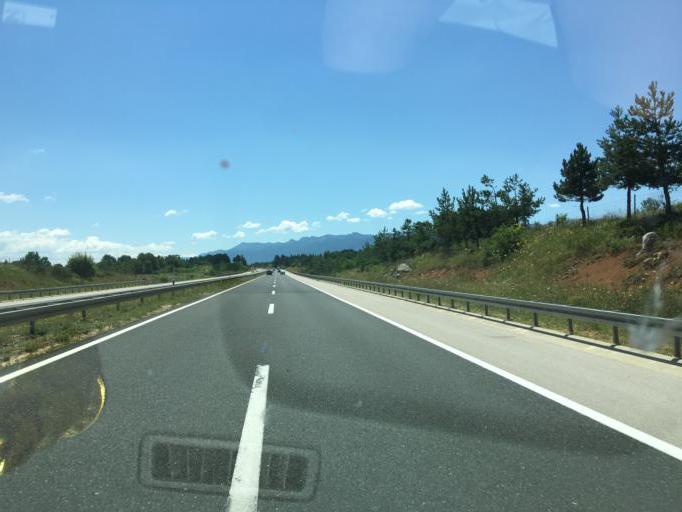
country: HR
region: Licko-Senjska
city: Gospic
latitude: 44.5484
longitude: 15.4341
